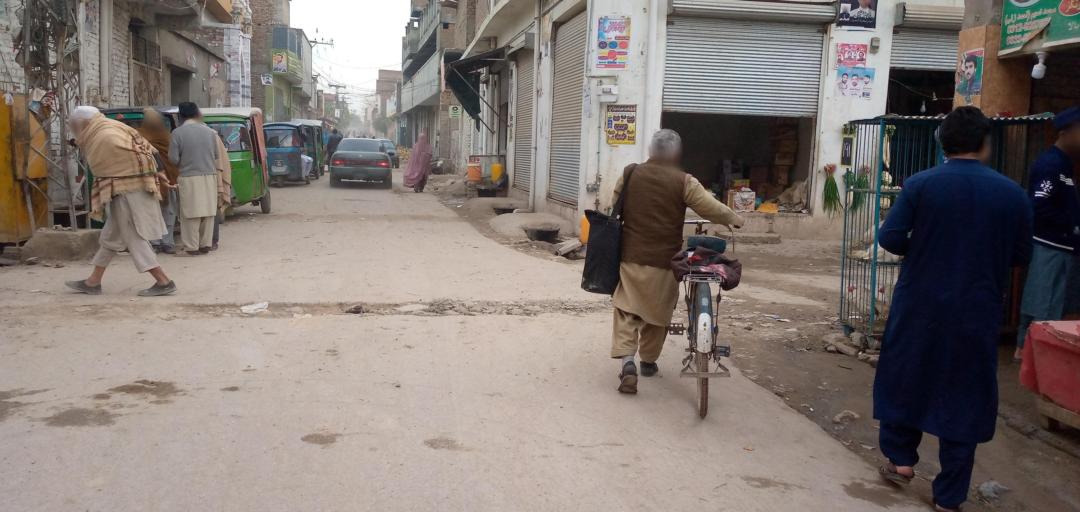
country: PK
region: Khyber Pakhtunkhwa
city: Peshawar
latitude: 34.0166
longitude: 71.4998
